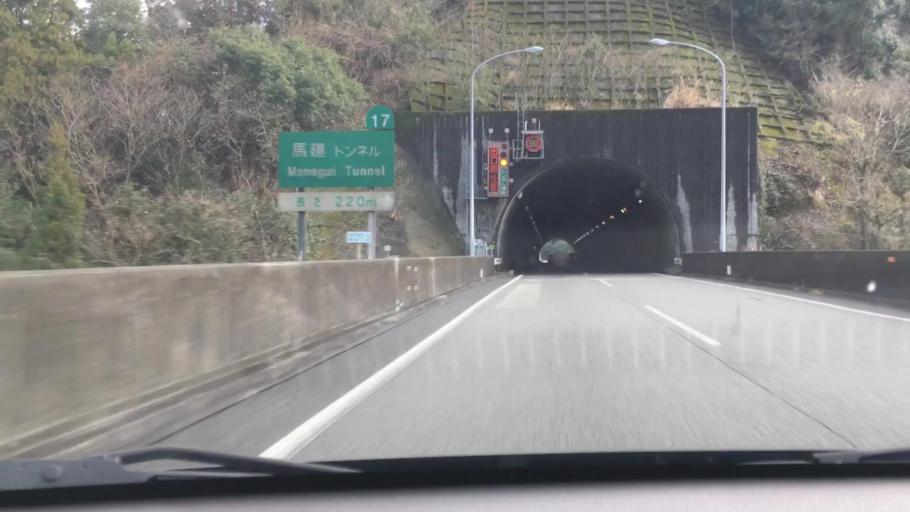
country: JP
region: Kumamoto
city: Yatsushiro
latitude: 32.4461
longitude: 130.6619
